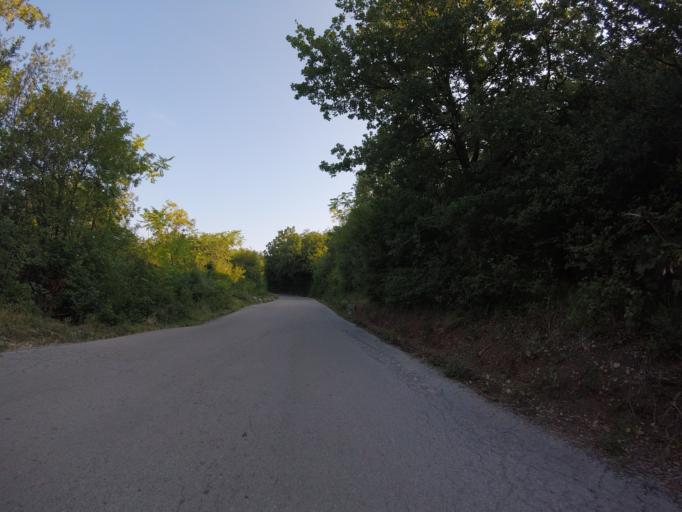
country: HR
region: Primorsko-Goranska
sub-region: Grad Crikvenica
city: Crikvenica
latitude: 45.1932
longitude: 14.7228
